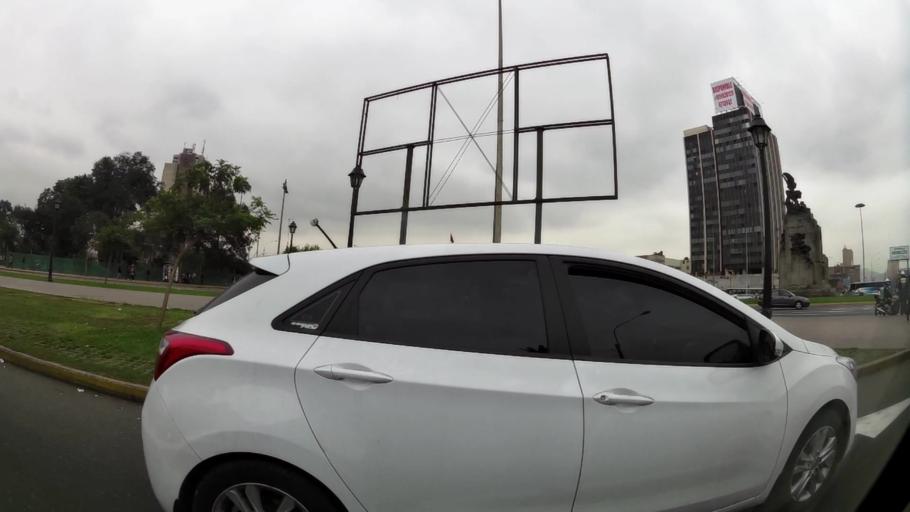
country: PE
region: Lima
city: Lima
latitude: -12.0600
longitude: -77.0365
